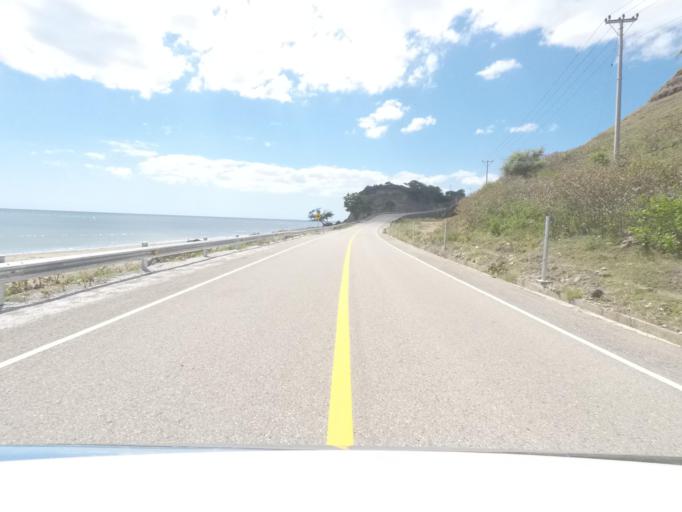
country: TL
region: Lautem
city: Lospalos
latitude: -8.4050
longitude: 126.8153
